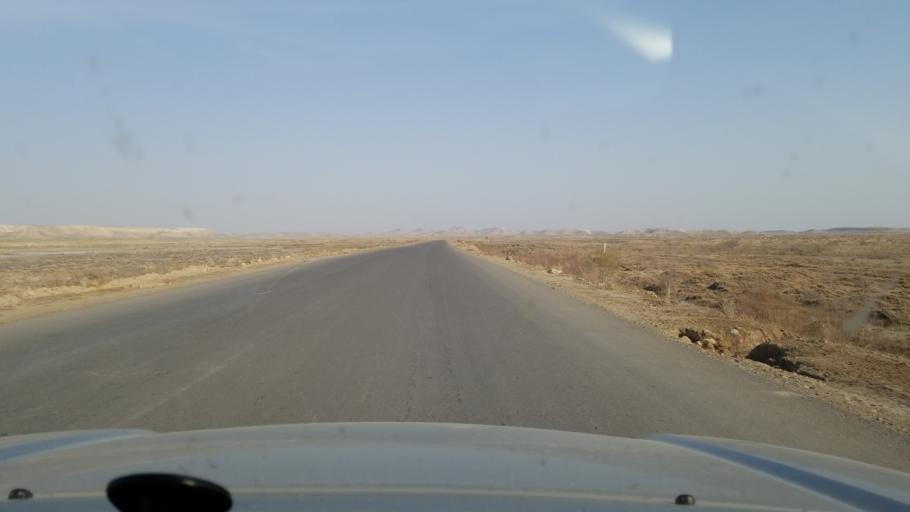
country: AF
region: Jowzjan
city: Khamyab
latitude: 37.6407
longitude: 65.6521
